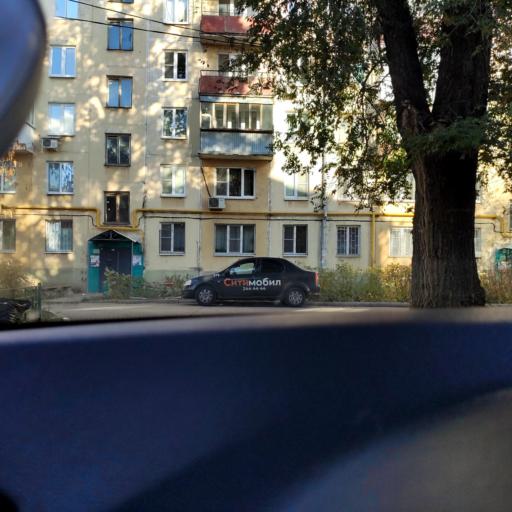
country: RU
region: Samara
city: Samara
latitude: 53.2084
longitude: 50.2483
